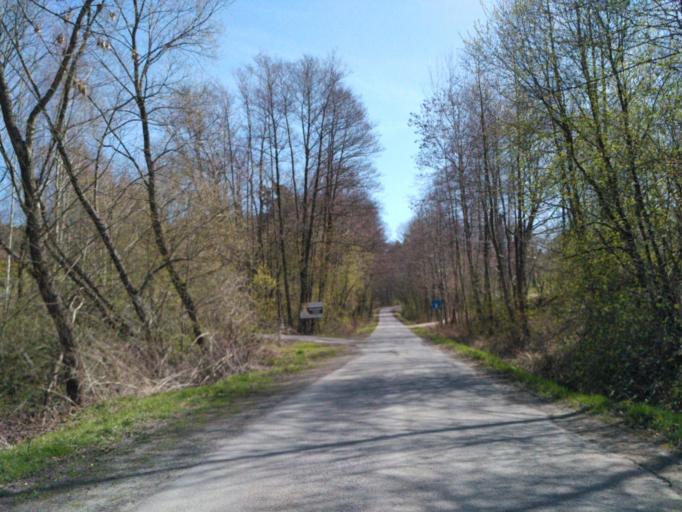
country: PL
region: Subcarpathian Voivodeship
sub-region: Powiat strzyzowski
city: Babica
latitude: 49.9270
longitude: 21.8851
